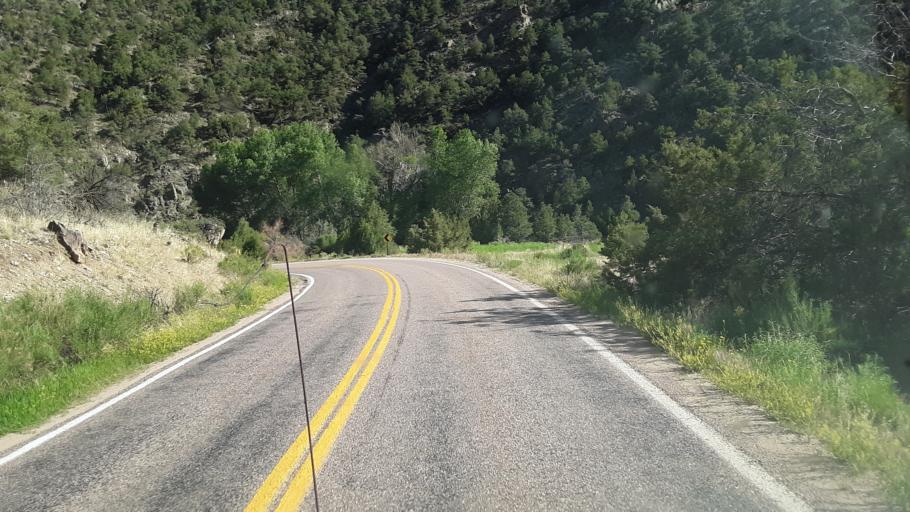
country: US
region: Colorado
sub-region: Fremont County
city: Canon City
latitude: 38.4320
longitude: -105.3925
